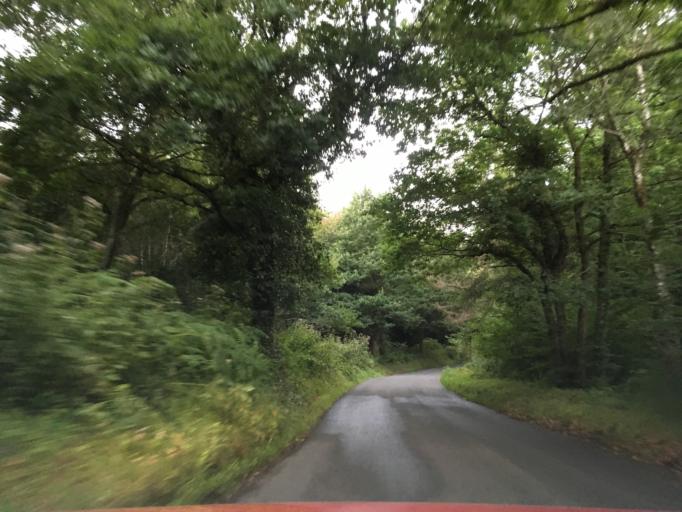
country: GB
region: Wales
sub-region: Newport
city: Llanvaches
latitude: 51.6458
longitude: -2.8342
